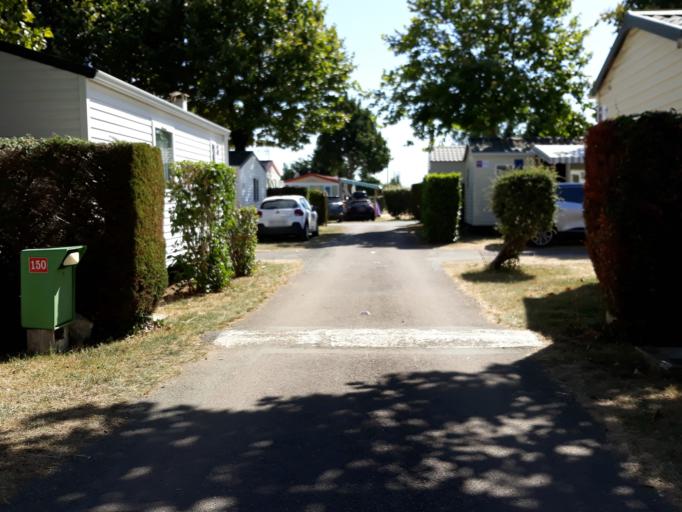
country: FR
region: Poitou-Charentes
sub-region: Departement de la Charente-Maritime
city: Saint-Laurent-de-la-Pree
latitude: 45.9873
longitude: -1.0536
